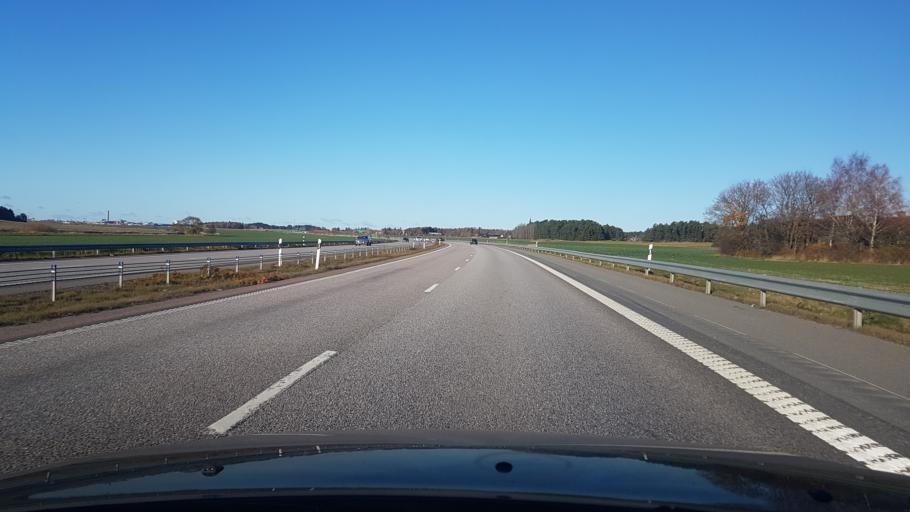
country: SE
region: Uppsala
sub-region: Uppsala Kommun
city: Saevja
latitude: 59.8180
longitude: 17.7537
